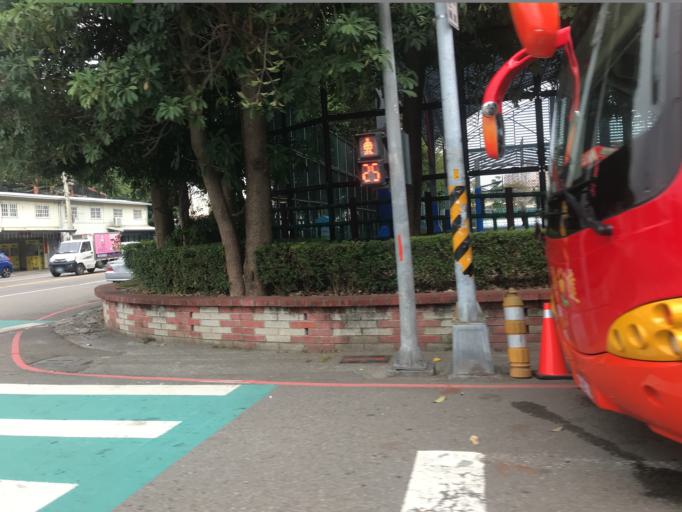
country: TW
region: Taiwan
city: Fengyuan
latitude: 24.3508
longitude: 120.6150
